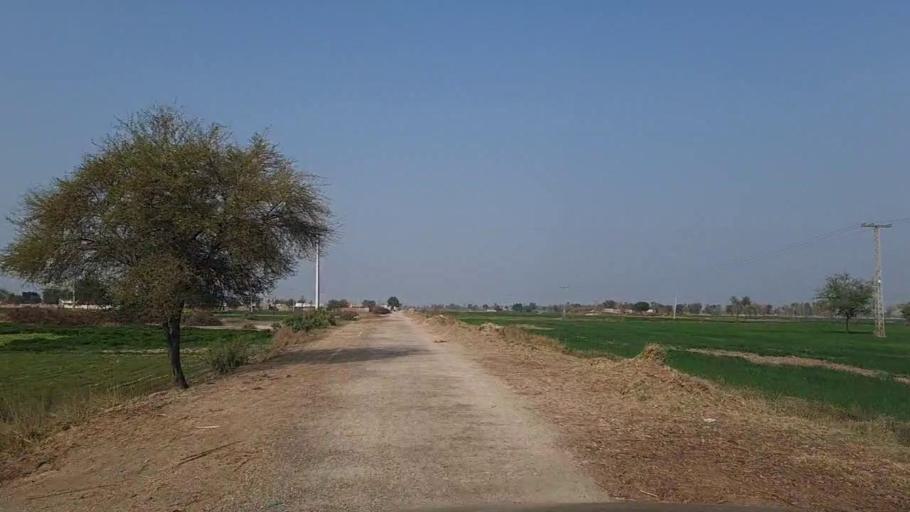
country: PK
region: Sindh
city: Daur
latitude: 26.4070
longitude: 68.4188
